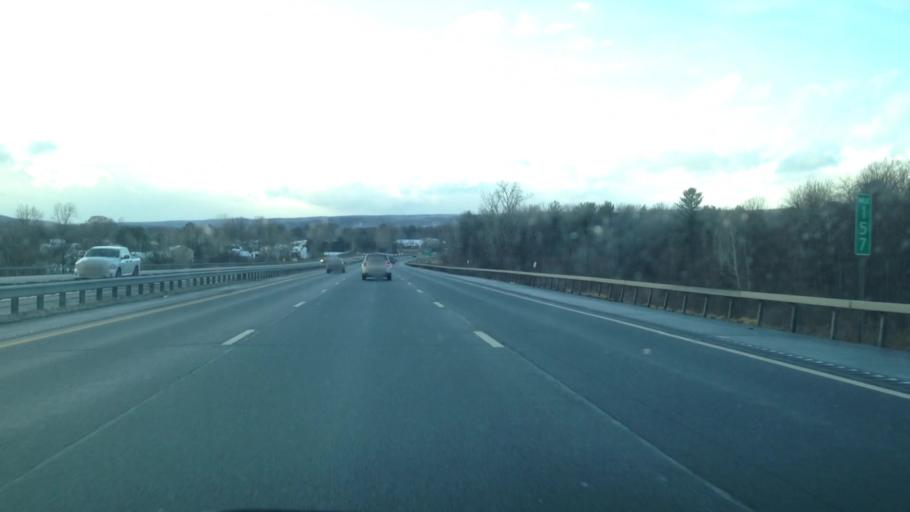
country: US
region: New York
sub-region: Schenectady County
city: Rotterdam
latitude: 42.7750
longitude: -73.9885
